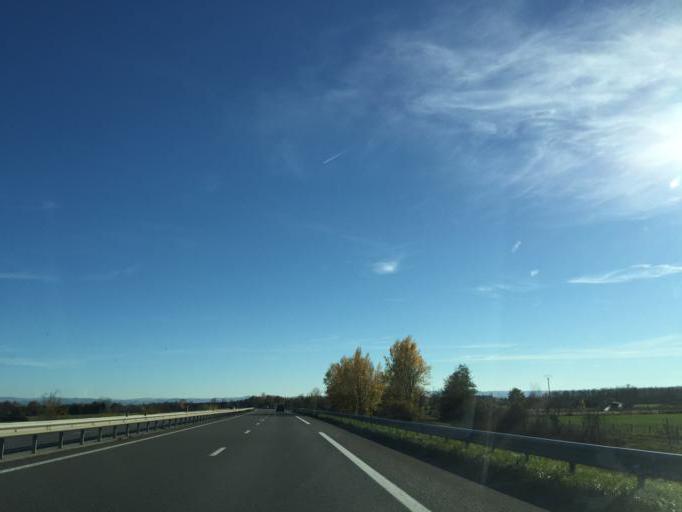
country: FR
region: Rhone-Alpes
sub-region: Departement de la Loire
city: Cuzieu
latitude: 45.5878
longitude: 4.2117
